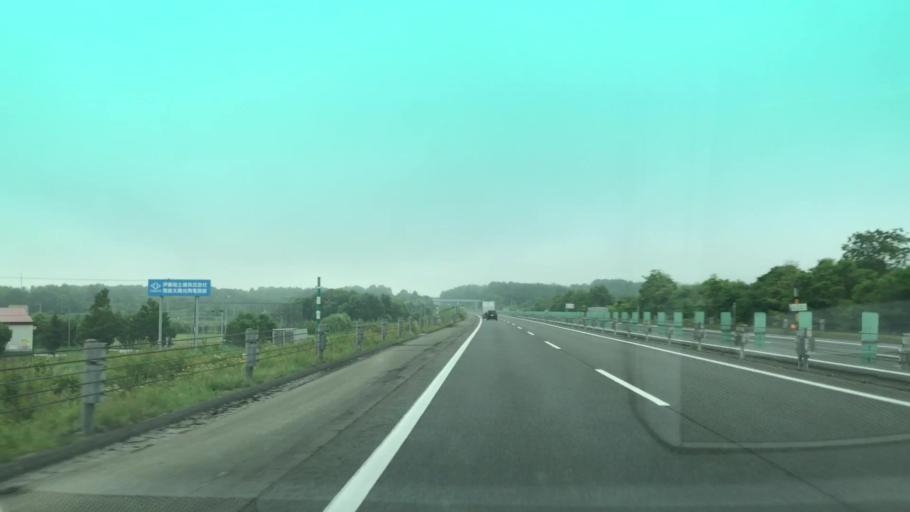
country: JP
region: Hokkaido
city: Kitahiroshima
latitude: 42.8942
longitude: 141.5497
